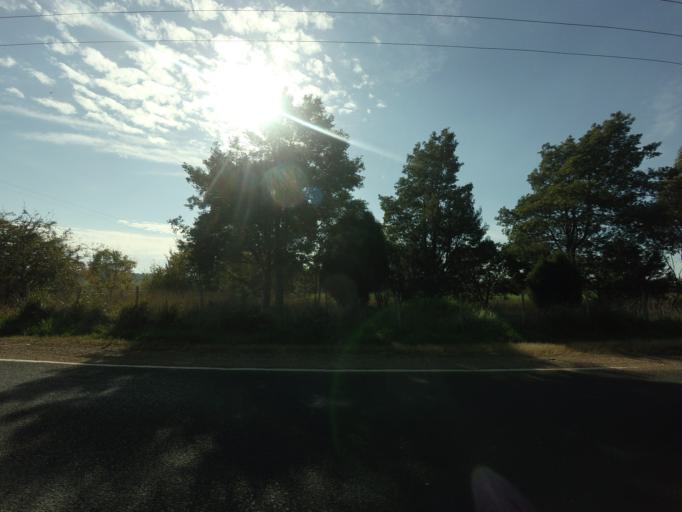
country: AU
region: Tasmania
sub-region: Northern Midlands
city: Longford
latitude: -41.5307
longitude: 146.9915
